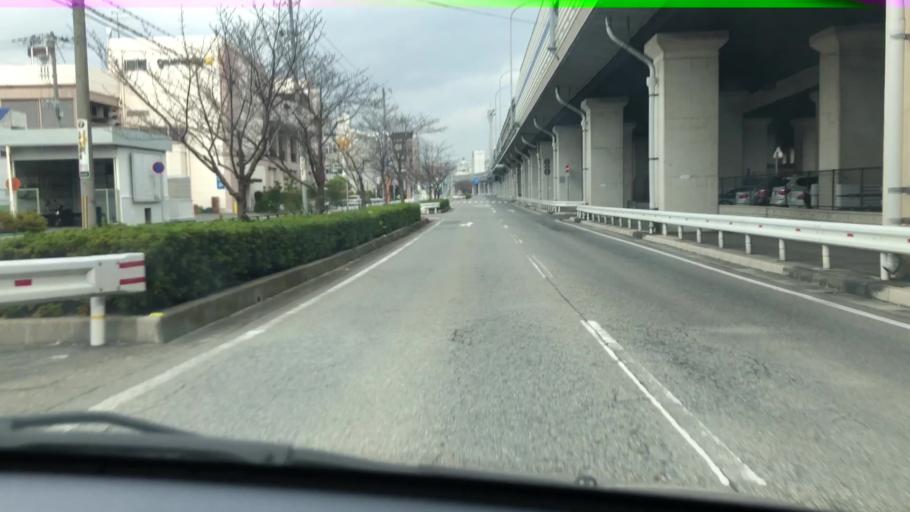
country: JP
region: Hyogo
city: Nishinomiya-hama
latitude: 34.7310
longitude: 135.3581
